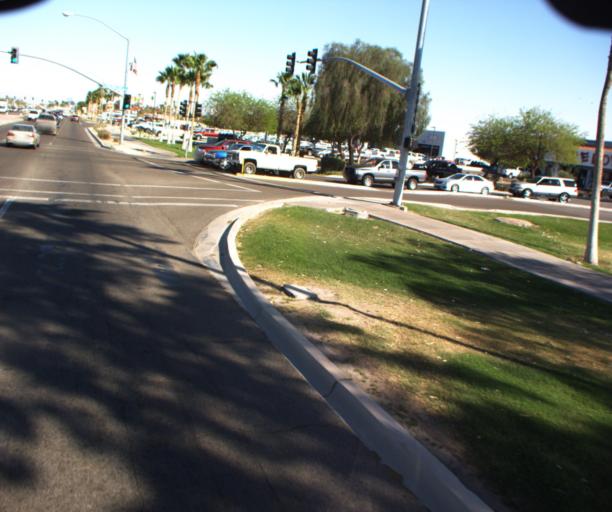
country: US
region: Arizona
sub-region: Yuma County
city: Yuma
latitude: 32.6694
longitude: -114.6200
